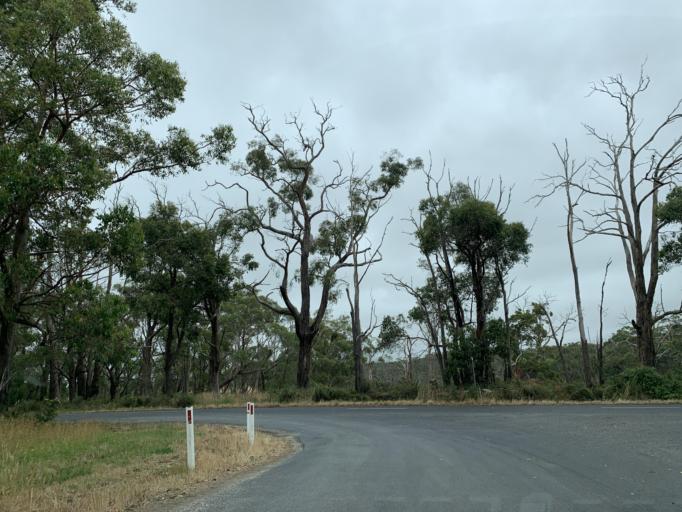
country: AU
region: Victoria
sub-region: Cardinia
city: Bunyip
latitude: -38.3292
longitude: 145.7059
